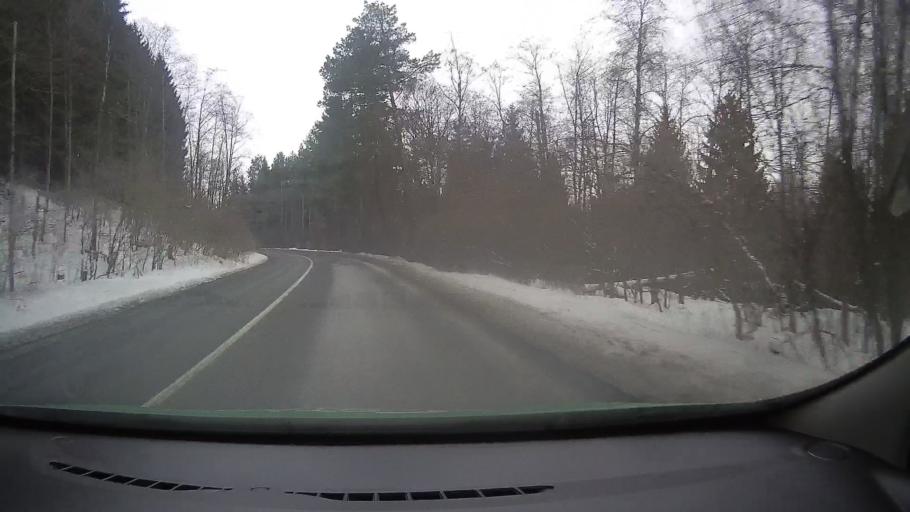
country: RO
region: Brasov
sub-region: Oras Predeal
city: Predeal
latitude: 45.5200
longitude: 25.5044
